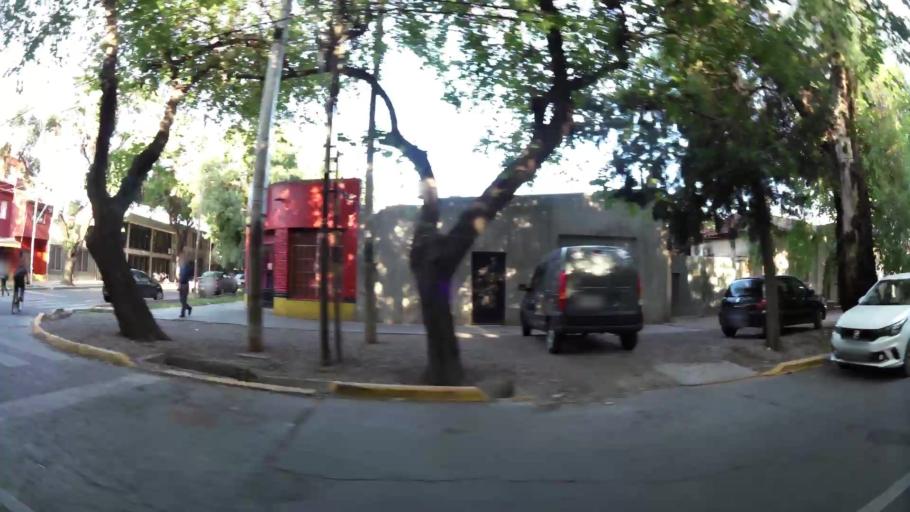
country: AR
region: Mendoza
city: Mendoza
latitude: -32.9005
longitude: -68.8405
